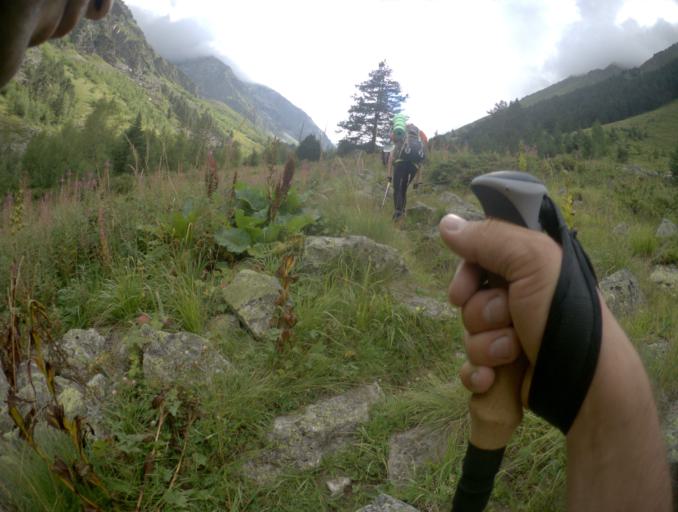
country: RU
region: Karachayevo-Cherkesiya
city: Uchkulan
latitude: 43.3431
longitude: 42.1422
